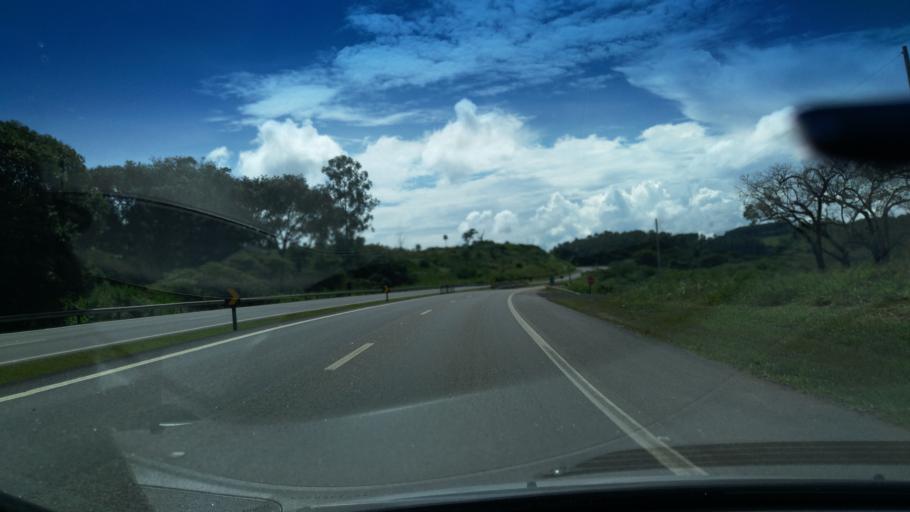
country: BR
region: Sao Paulo
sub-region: Santo Antonio Do Jardim
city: Espirito Santo do Pinhal
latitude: -22.2226
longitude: -46.7920
